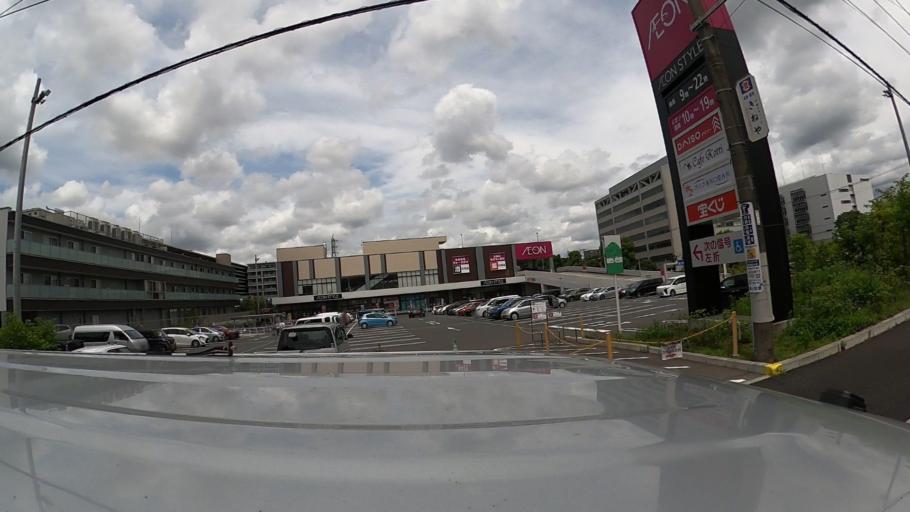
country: JP
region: Kanagawa
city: Fujisawa
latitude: 35.4088
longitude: 139.5392
